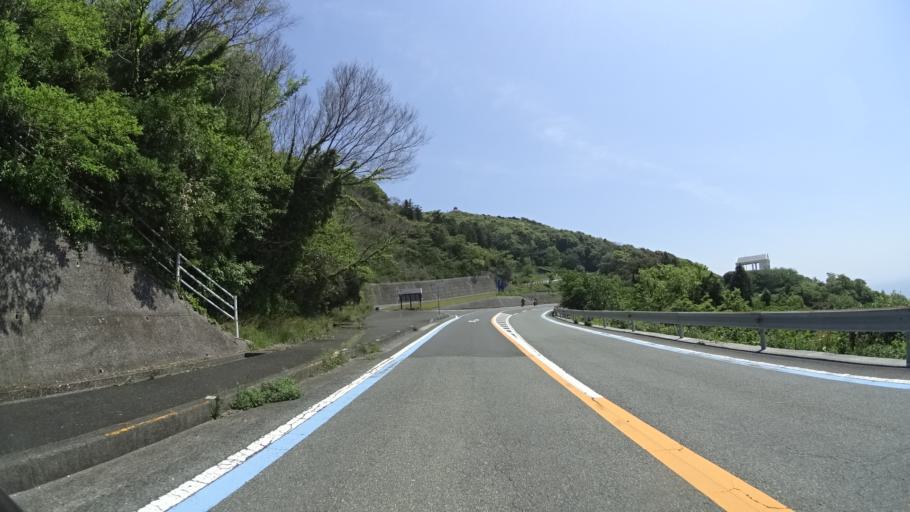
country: JP
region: Ehime
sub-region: Nishiuwa-gun
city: Ikata-cho
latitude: 33.4199
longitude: 132.1936
